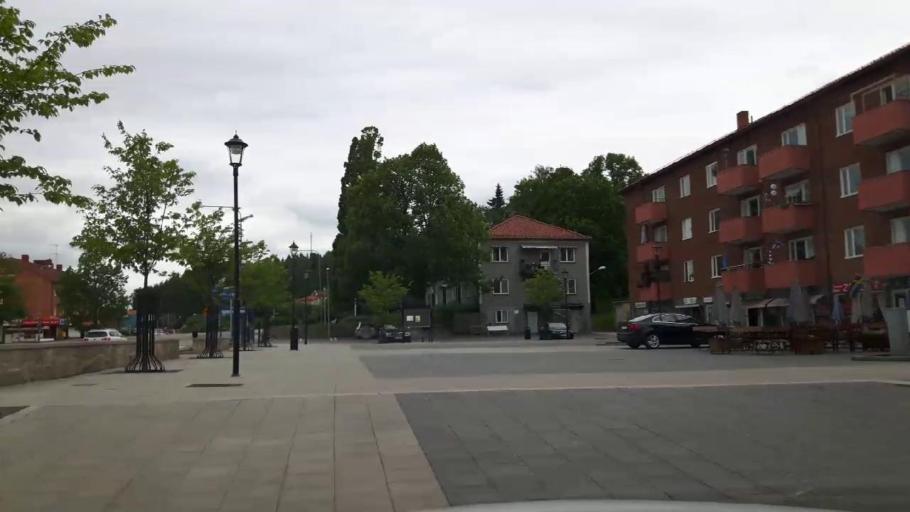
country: SE
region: Vaestmanland
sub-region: Kopings Kommun
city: Kolsva
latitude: 59.5998
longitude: 15.8431
